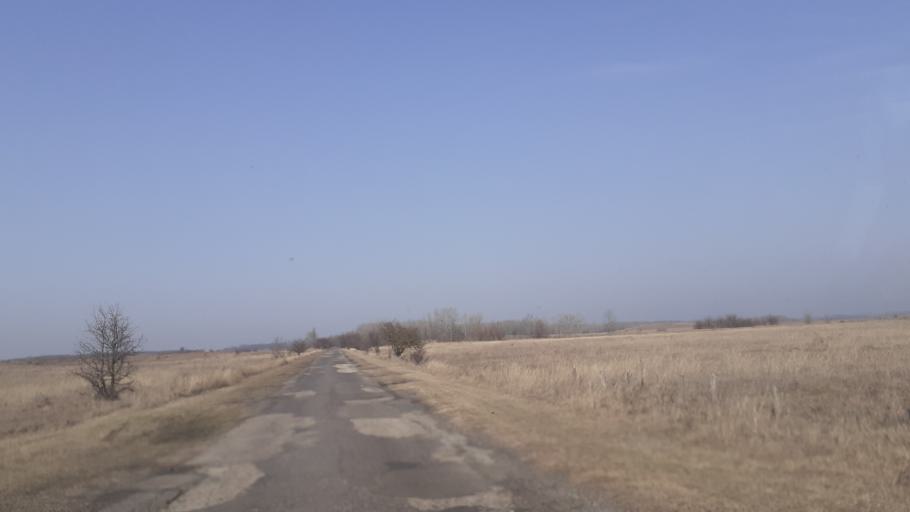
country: HU
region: Pest
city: Dabas
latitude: 47.1044
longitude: 19.2259
